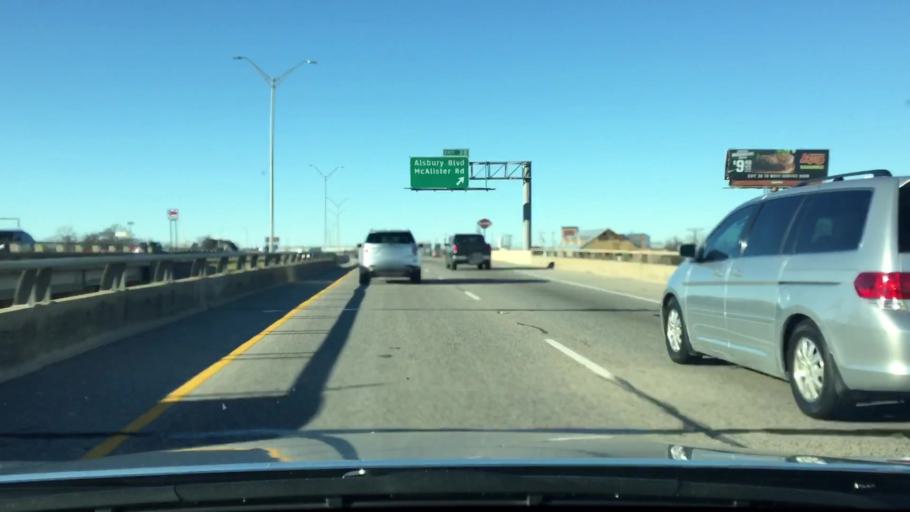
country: US
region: Texas
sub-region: Johnson County
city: Burleson
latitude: 32.5437
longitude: -97.3147
